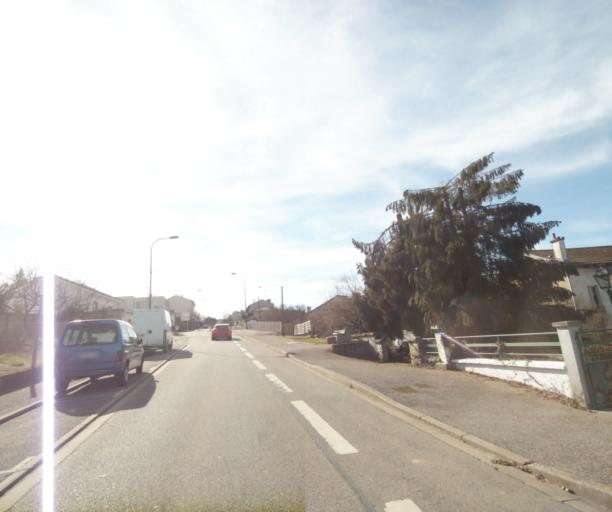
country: FR
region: Lorraine
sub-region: Departement de Meurthe-et-Moselle
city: Villers-les-Nancy
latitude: 48.6689
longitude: 6.1396
